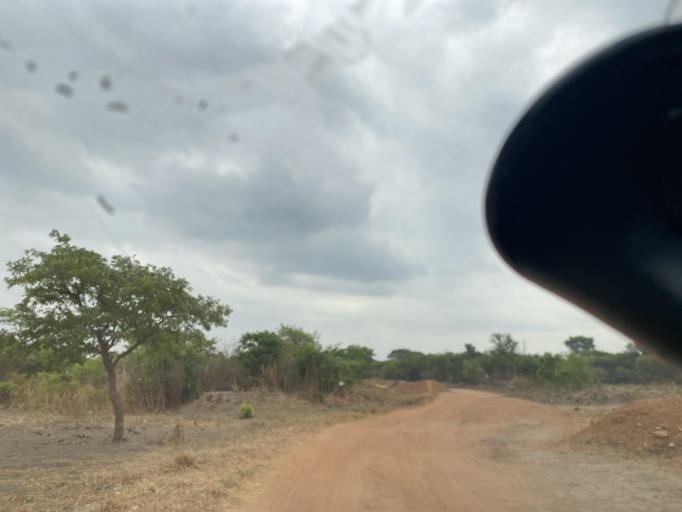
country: ZM
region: Lusaka
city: Chongwe
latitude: -15.2441
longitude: 28.7239
